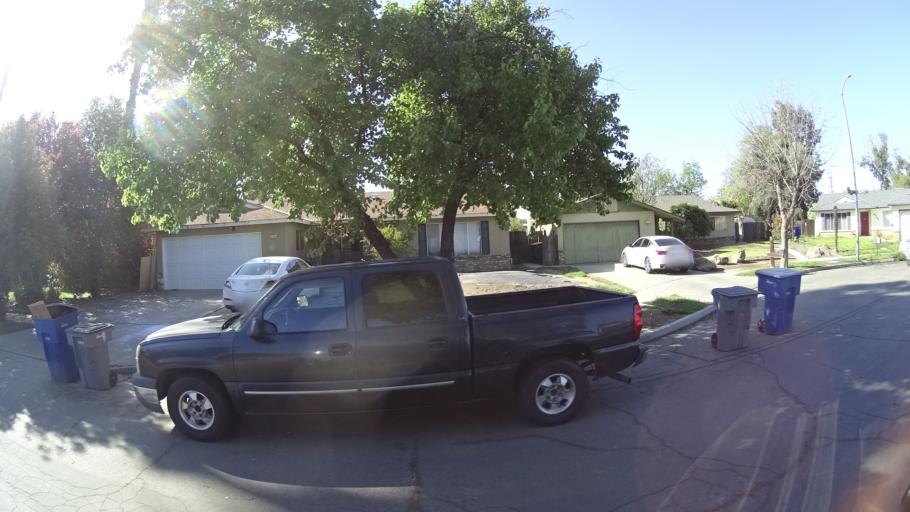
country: US
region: California
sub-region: Fresno County
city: West Park
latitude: 36.7945
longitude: -119.8791
